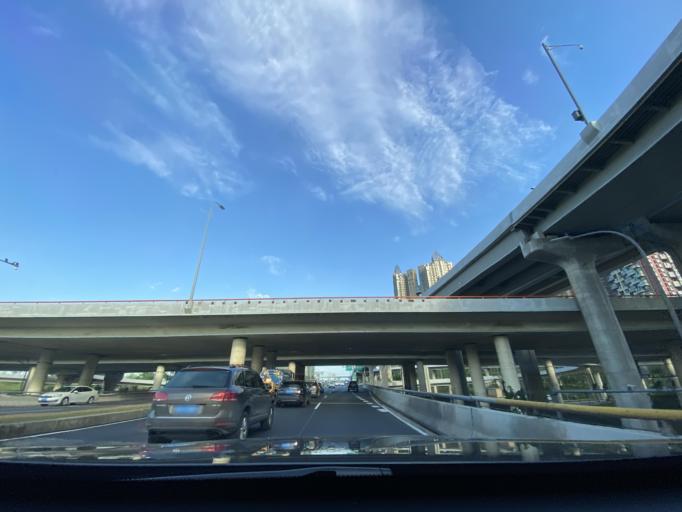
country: CN
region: Sichuan
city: Chengdu
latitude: 30.6368
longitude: 104.1488
